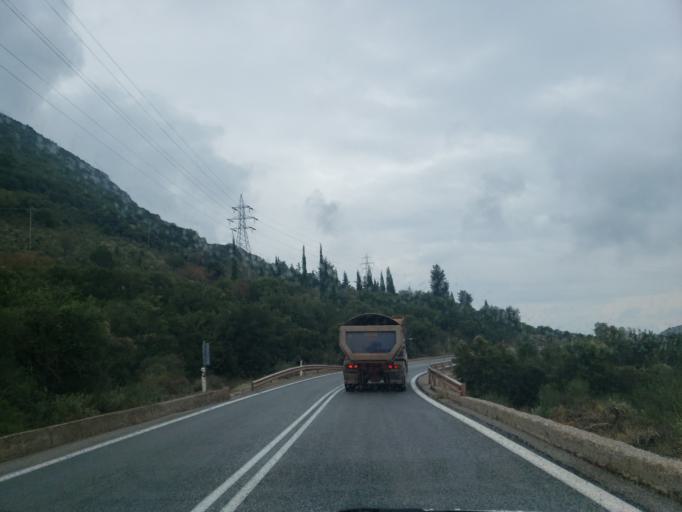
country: GR
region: Central Greece
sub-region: Nomos Fokidos
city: Amfissa
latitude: 38.5729
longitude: 22.3966
